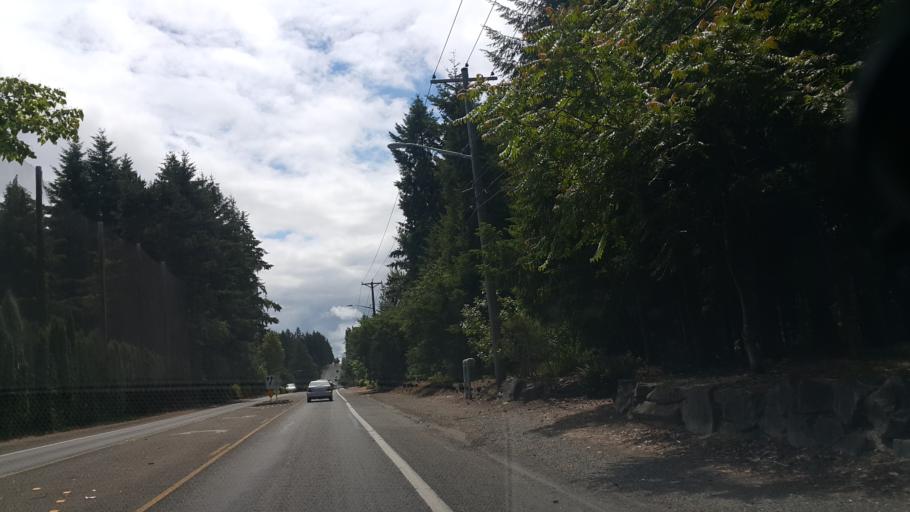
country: US
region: Washington
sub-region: Pierce County
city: Fircrest
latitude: 47.2308
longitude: -122.5263
